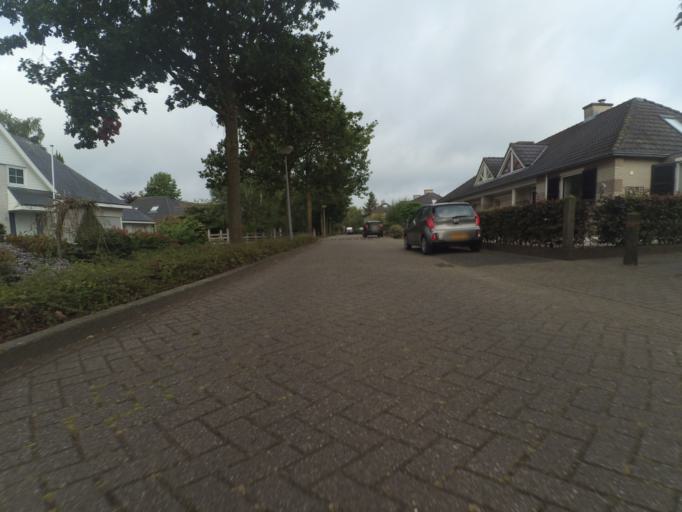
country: NL
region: Utrecht
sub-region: Gemeente Utrechtse Heuvelrug
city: Overberg
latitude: 52.0794
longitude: 5.4979
